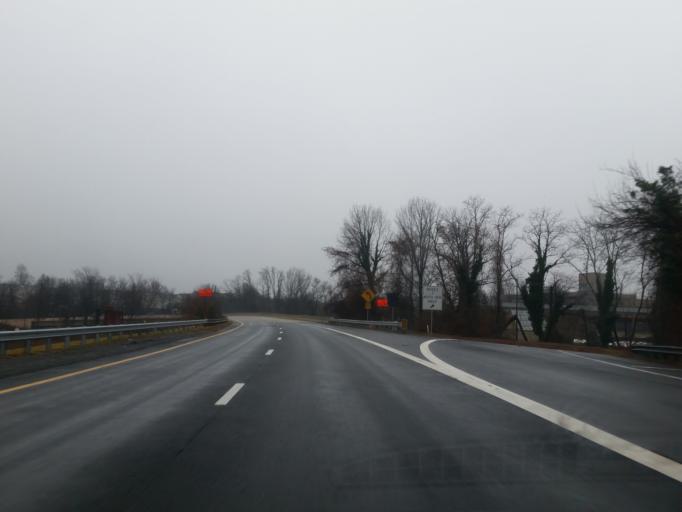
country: US
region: Virginia
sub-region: Fairfax County
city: Pimmit Hills
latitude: 38.9027
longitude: -77.1885
